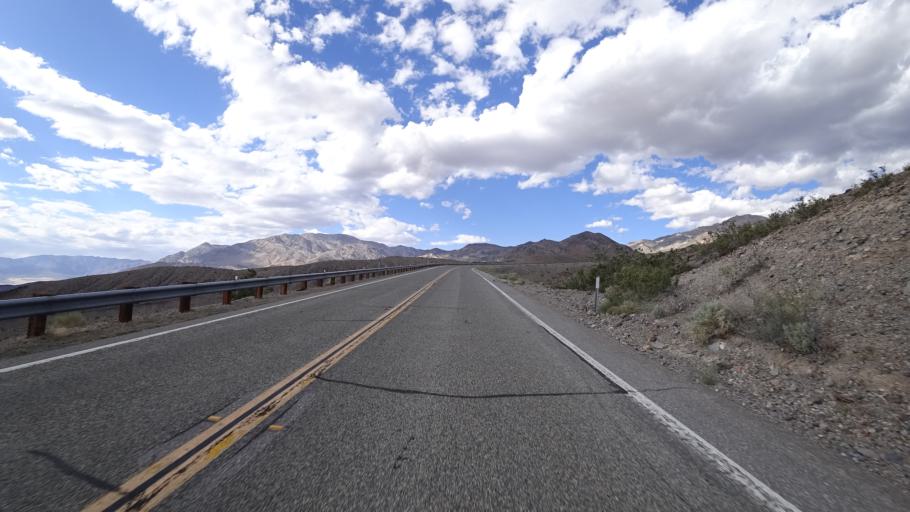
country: US
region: California
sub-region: San Bernardino County
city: Searles Valley
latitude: 36.3446
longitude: -117.3092
